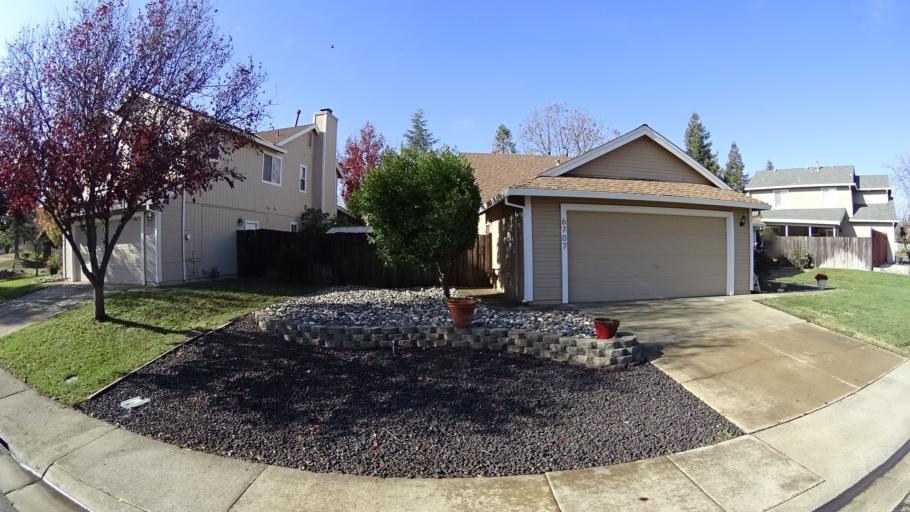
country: US
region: California
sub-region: Sacramento County
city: Antelope
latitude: 38.6883
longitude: -121.3272
